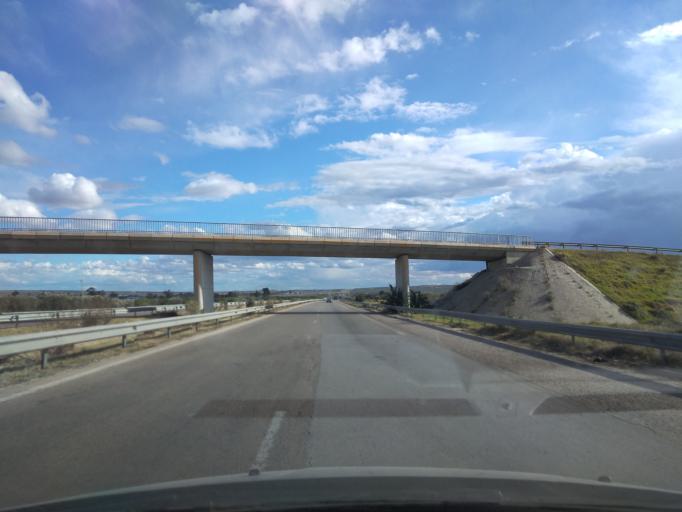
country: TN
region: Al Munastir
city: Manzil Kamil
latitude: 35.5916
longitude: 10.6045
